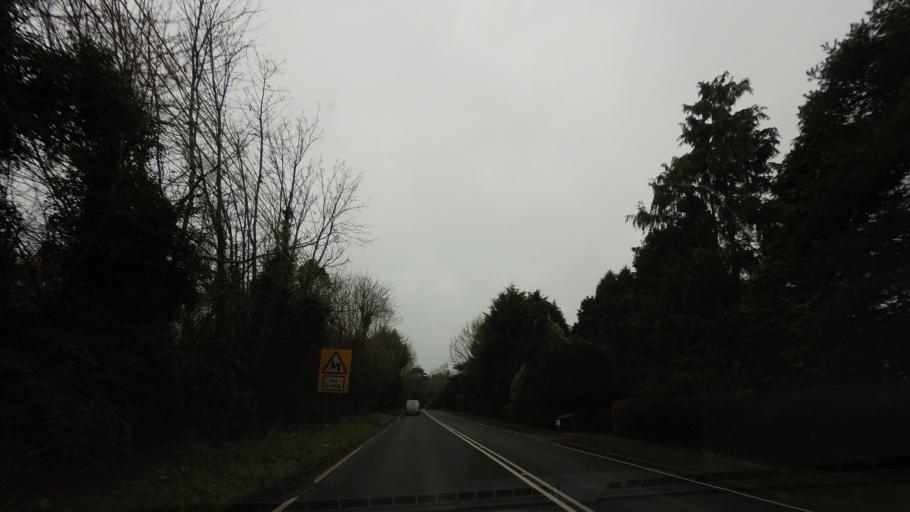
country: GB
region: England
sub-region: East Sussex
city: Battle
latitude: 50.9501
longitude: 0.5055
